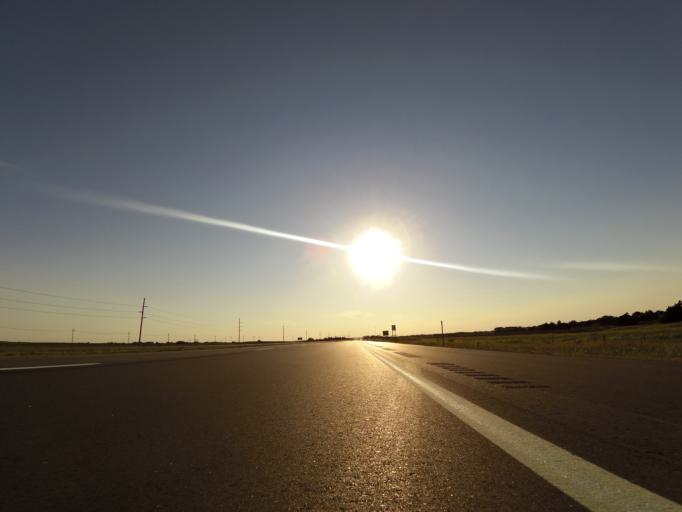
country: US
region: Kansas
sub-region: Reno County
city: South Hutchinson
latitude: 38.0133
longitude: -97.9505
